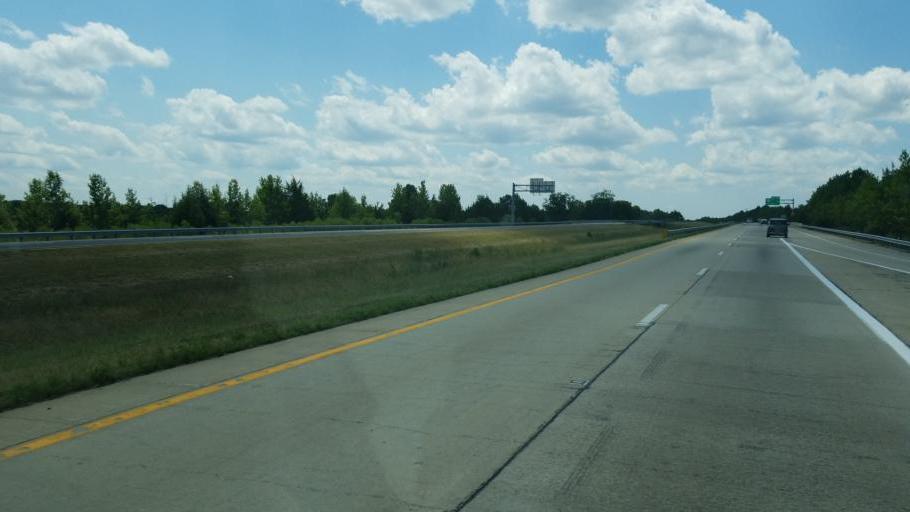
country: US
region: Virginia
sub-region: Prince George County
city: Prince George
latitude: 37.1939
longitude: -77.3259
